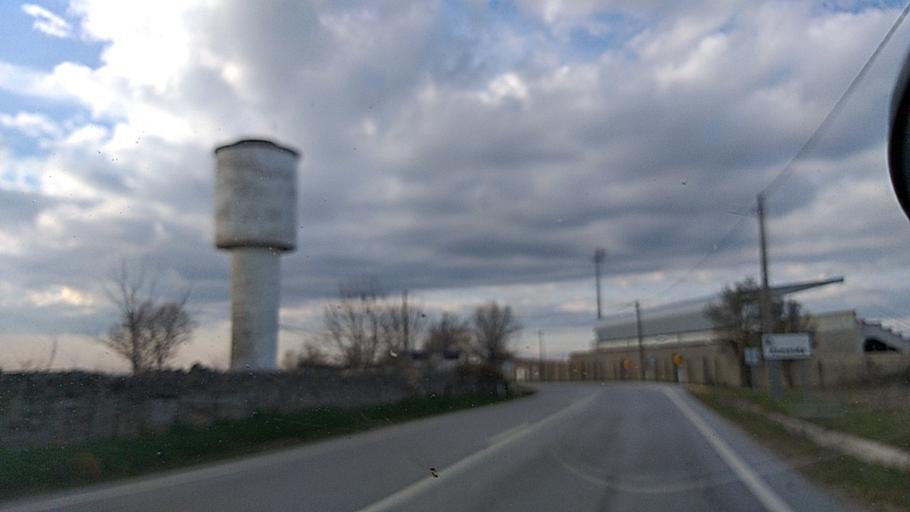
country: ES
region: Castille and Leon
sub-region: Provincia de Salamanca
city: Aldea del Obispo
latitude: 40.7118
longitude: -6.8983
